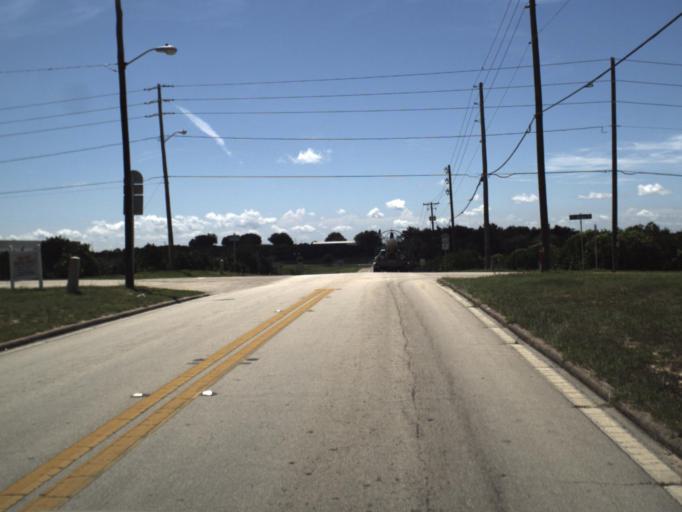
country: US
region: Florida
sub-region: Polk County
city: Frostproof
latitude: 27.7301
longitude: -81.5310
